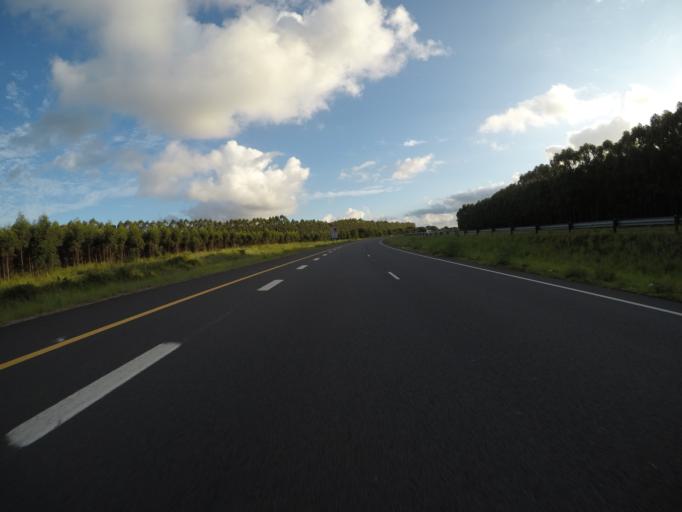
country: ZA
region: KwaZulu-Natal
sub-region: uThungulu District Municipality
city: KwaMbonambi
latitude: -28.5260
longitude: 32.1382
